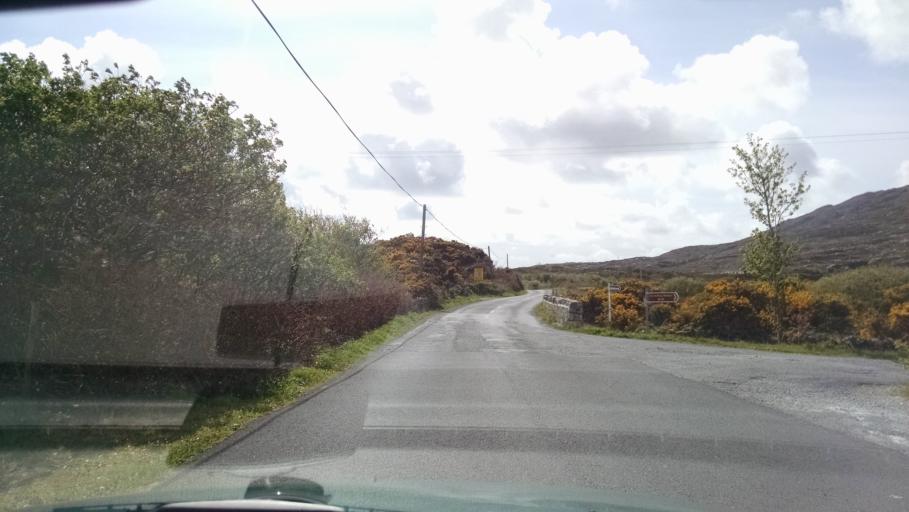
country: IE
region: Connaught
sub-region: County Galway
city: Clifden
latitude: 53.3910
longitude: -9.9283
